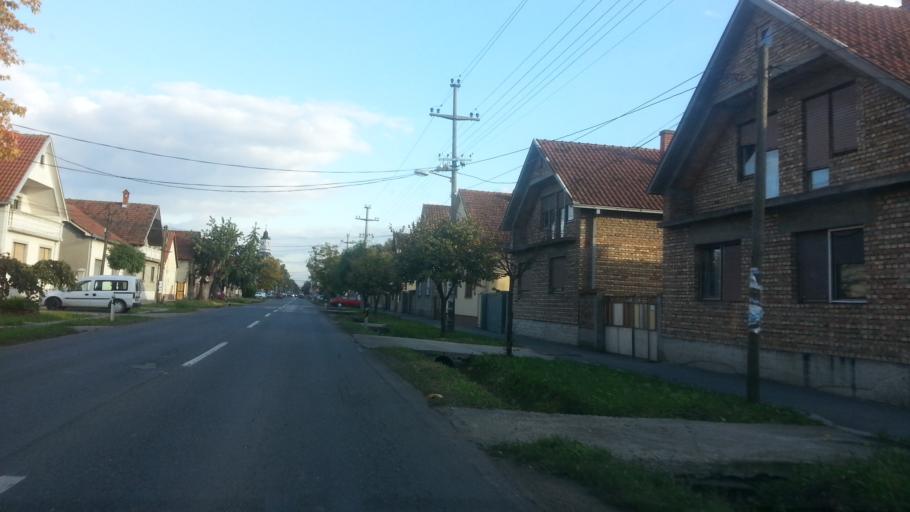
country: RS
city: Novi Banovci
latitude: 44.9083
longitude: 20.2710
